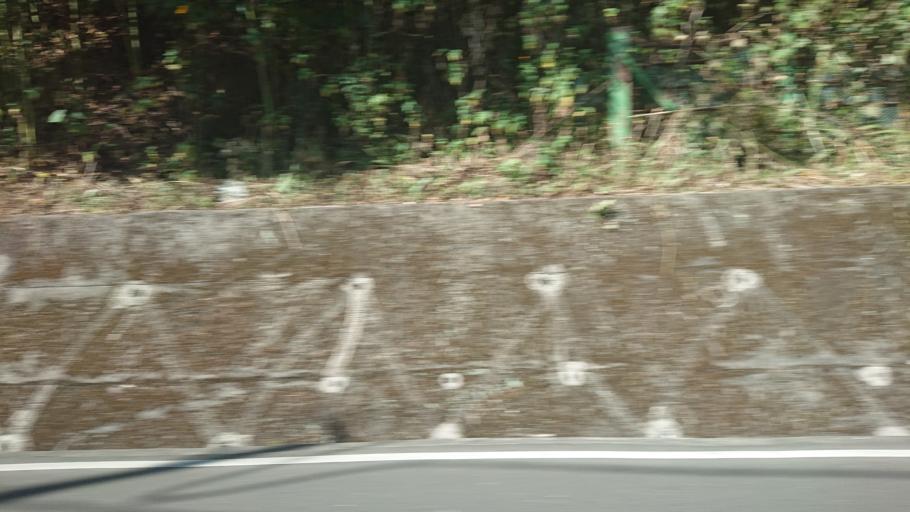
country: TW
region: Taiwan
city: Lugu
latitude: 23.4674
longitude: 120.7303
